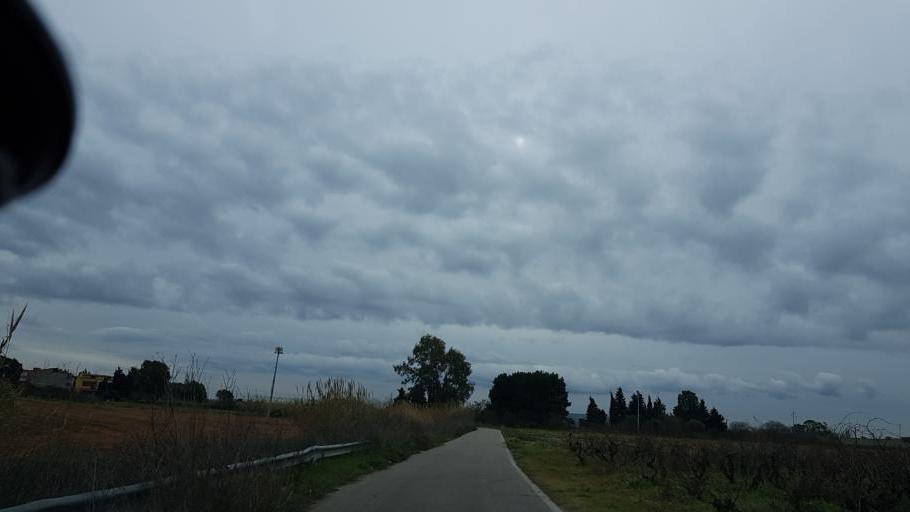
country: IT
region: Apulia
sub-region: Provincia di Brindisi
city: La Rosa
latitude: 40.6130
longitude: 17.9508
